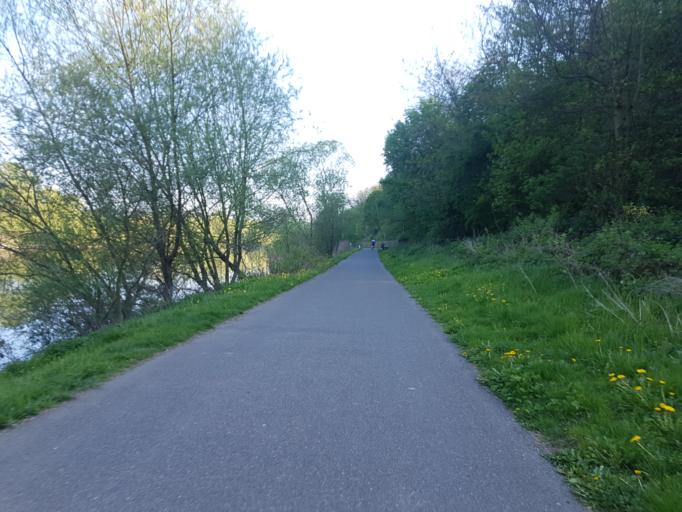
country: DE
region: North Rhine-Westphalia
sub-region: Regierungsbezirk Dusseldorf
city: Essen
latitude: 51.4354
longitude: 7.0849
